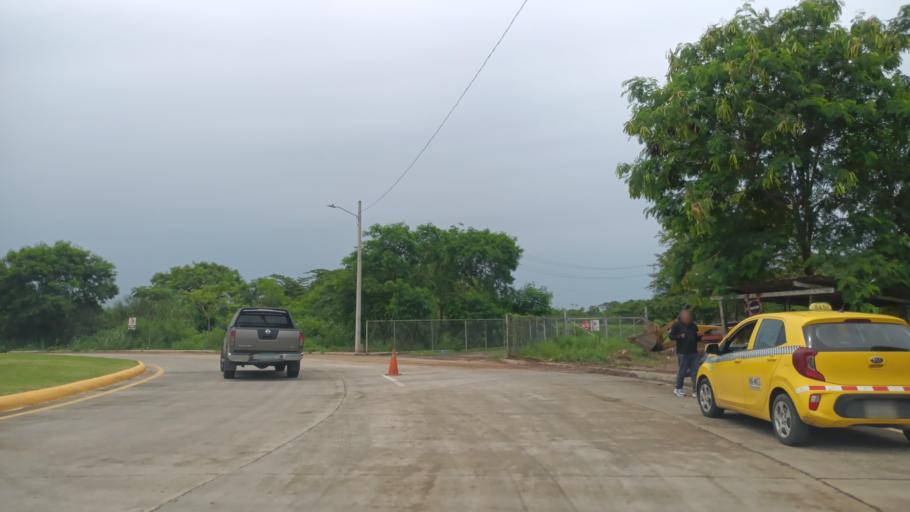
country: PA
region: Panama
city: Tocumen
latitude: 9.0372
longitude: -79.4045
